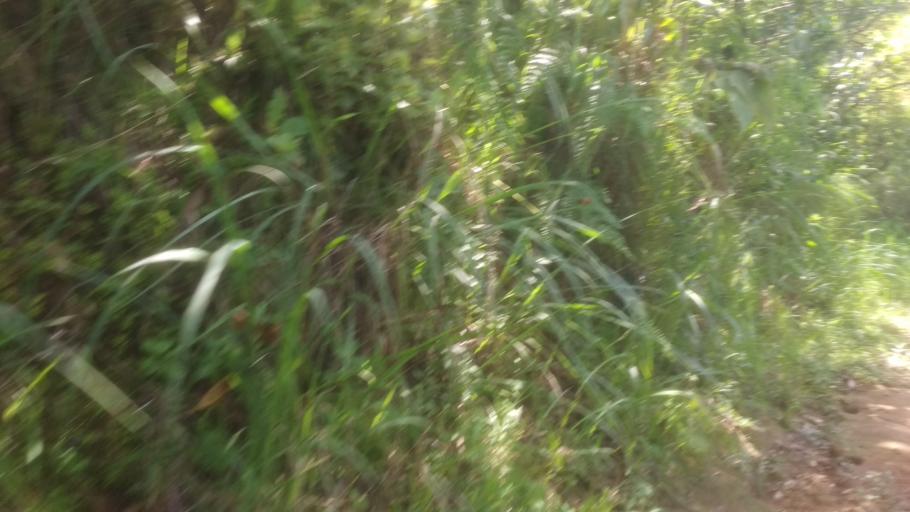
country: IN
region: Kerala
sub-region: Idukki
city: Idukki
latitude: 9.9781
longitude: 76.8351
